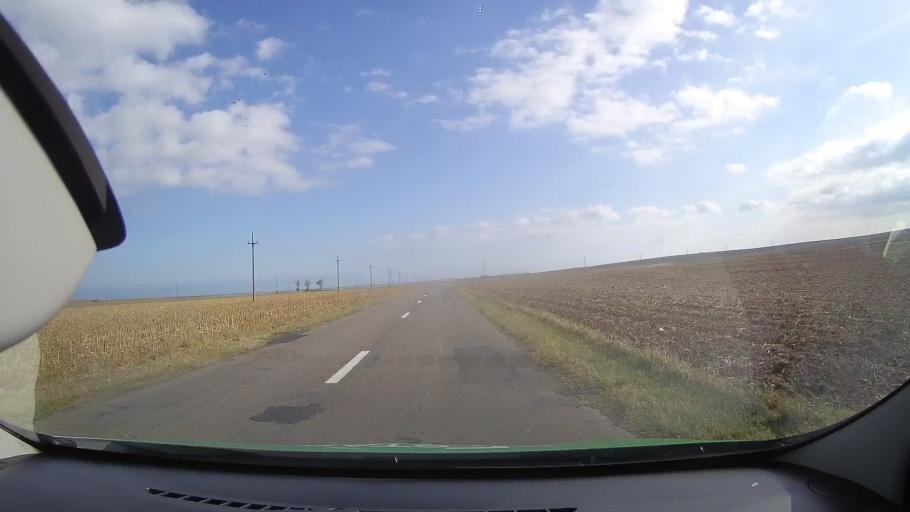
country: RO
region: Constanta
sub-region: Comuna Istria
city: Nuntasi
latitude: 44.5321
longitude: 28.6725
